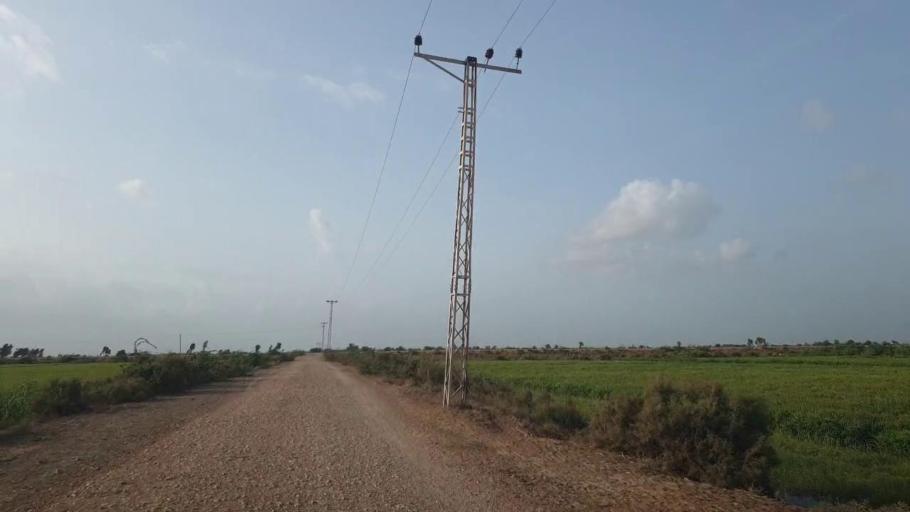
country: PK
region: Sindh
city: Tando Bago
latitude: 24.6541
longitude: 69.1119
